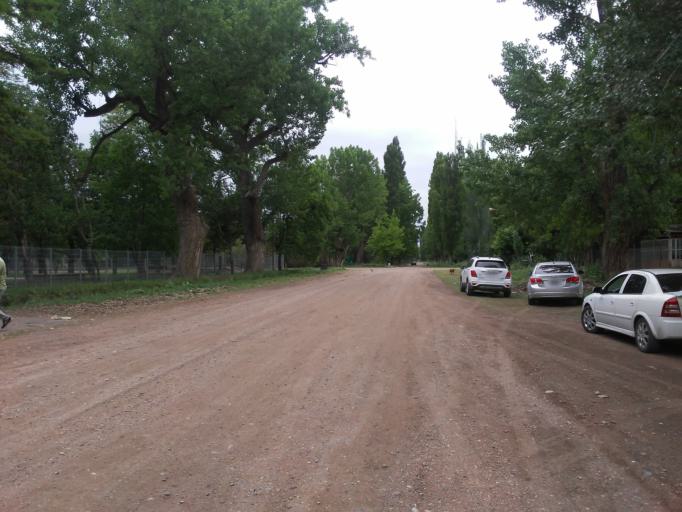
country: AR
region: Mendoza
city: San Rafael
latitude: -34.5879
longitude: -68.5499
